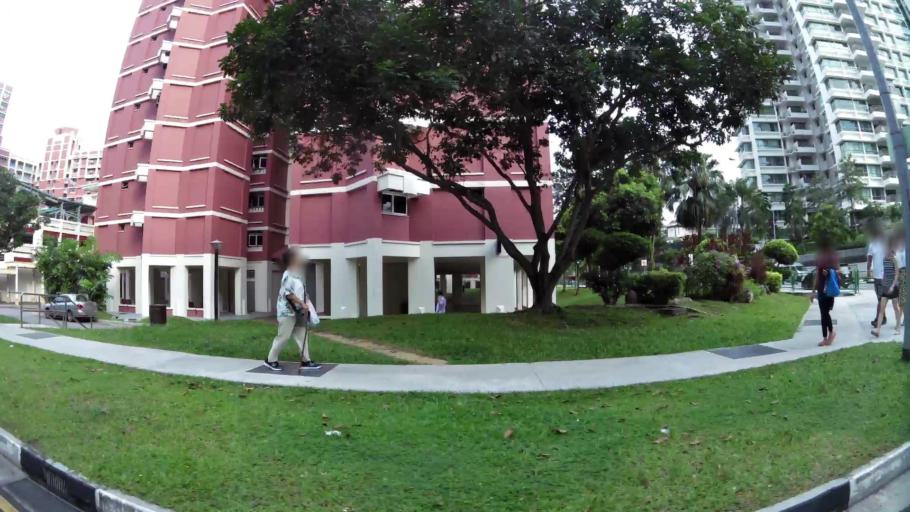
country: SG
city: Singapore
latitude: 1.3387
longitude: 103.8466
